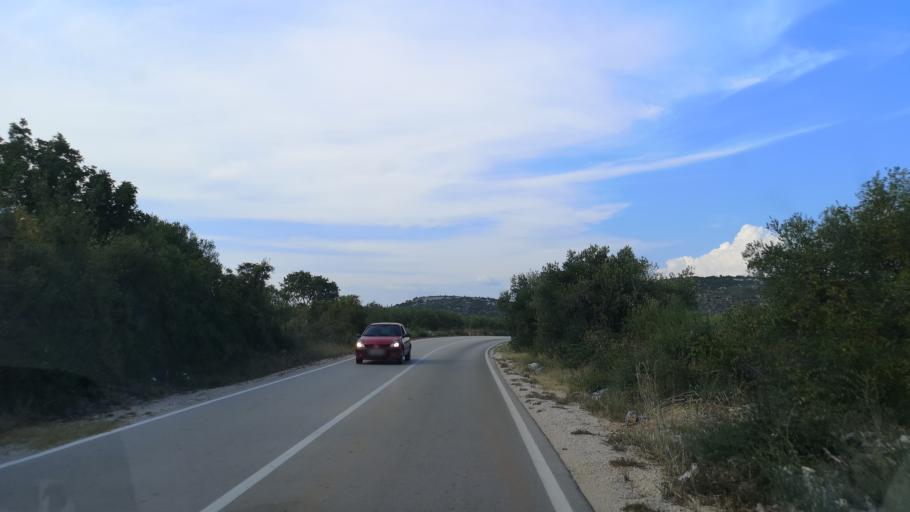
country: HR
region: Sibensko-Kniniska
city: Zaton
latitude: 43.8204
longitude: 15.7789
